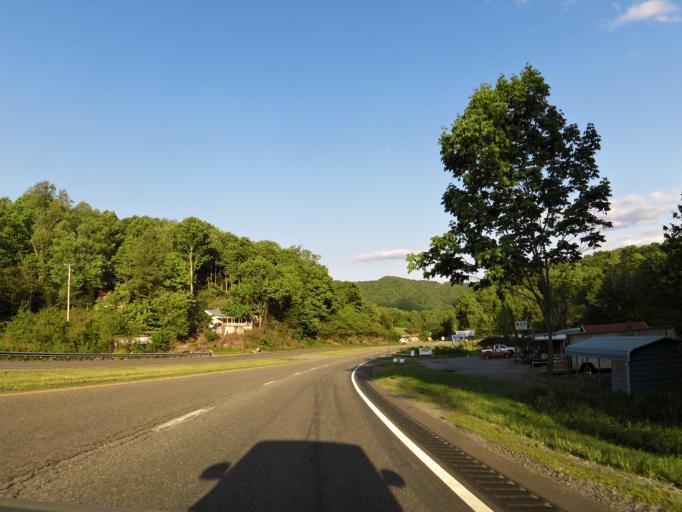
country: US
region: Virginia
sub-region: Russell County
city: Lebanon
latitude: 36.8156
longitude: -82.1130
